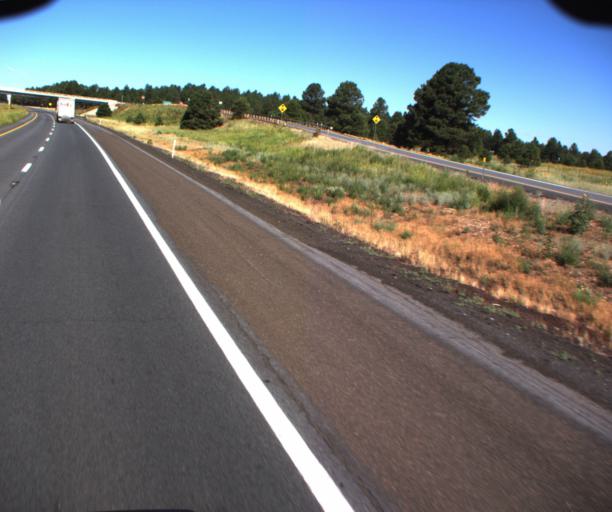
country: US
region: Arizona
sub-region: Coconino County
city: Parks
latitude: 35.2643
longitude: -112.0474
